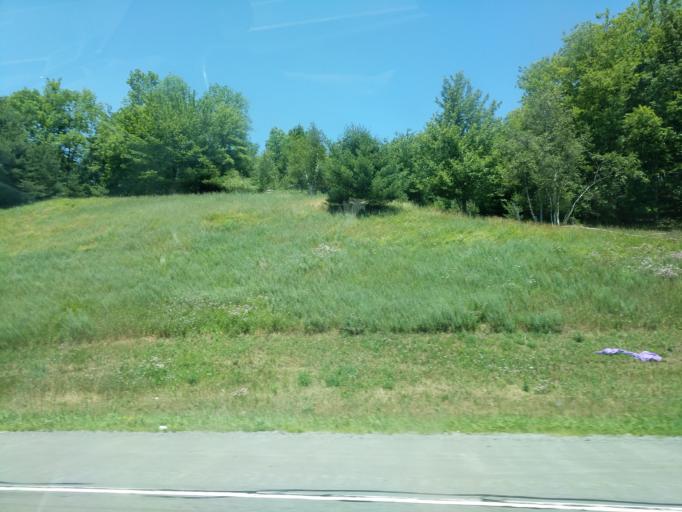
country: US
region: New York
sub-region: Sullivan County
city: Rock Hill
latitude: 41.6294
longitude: -74.6085
